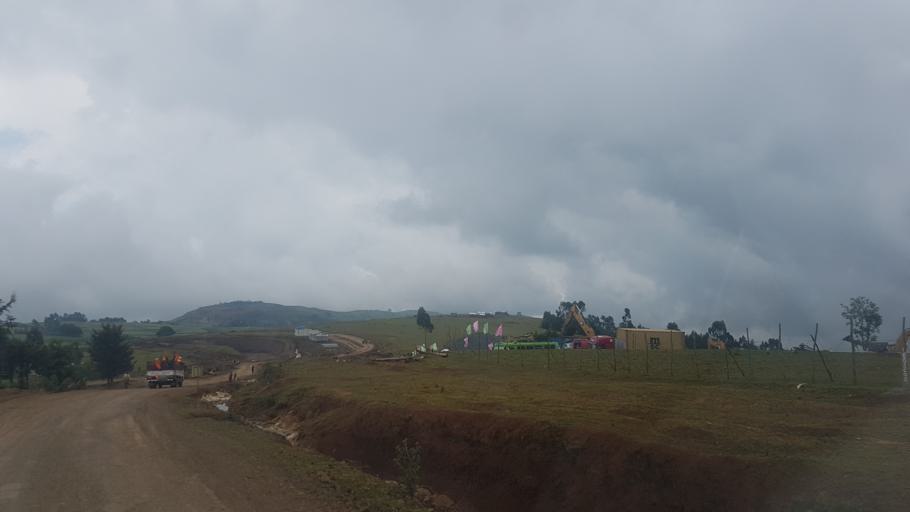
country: ET
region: Southern Nations, Nationalities, and People's Region
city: Arba Minch'
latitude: 6.3257
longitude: 37.5474
